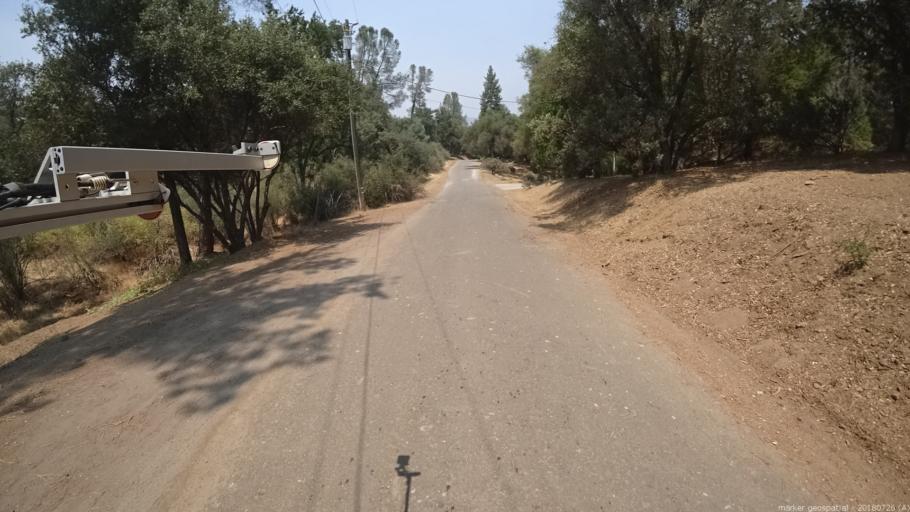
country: US
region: California
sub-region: Madera County
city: Oakhurst
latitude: 37.3206
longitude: -119.6450
